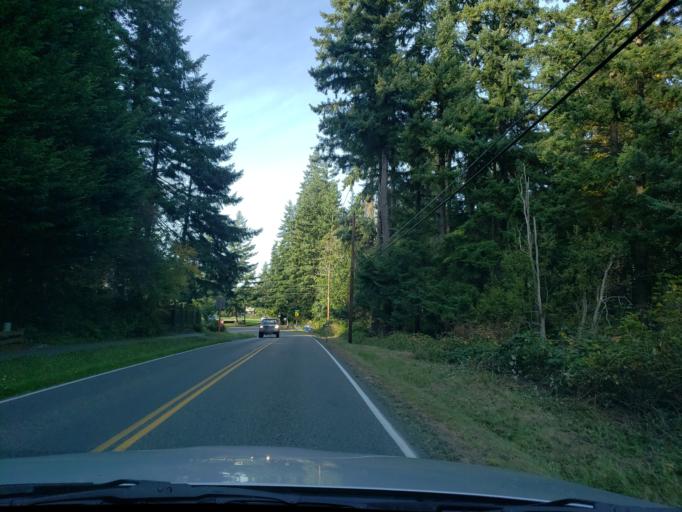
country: US
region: Washington
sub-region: Snohomish County
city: Mukilteo
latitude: 47.9285
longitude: -122.2933
